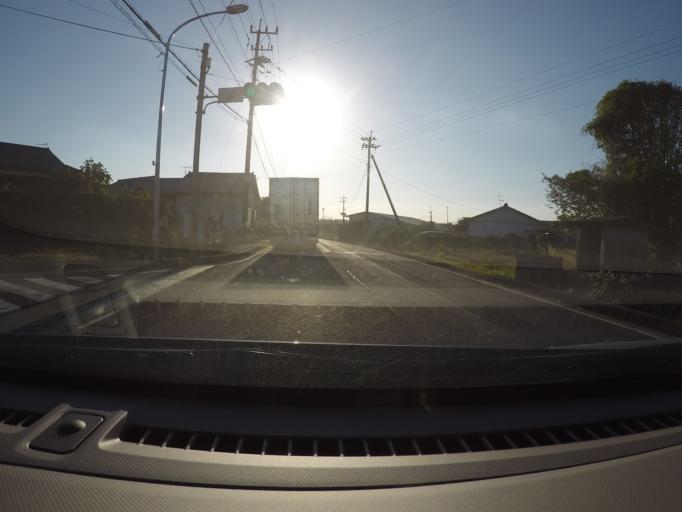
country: JP
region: Kagoshima
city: Izumi
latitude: 32.0846
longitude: 130.2789
